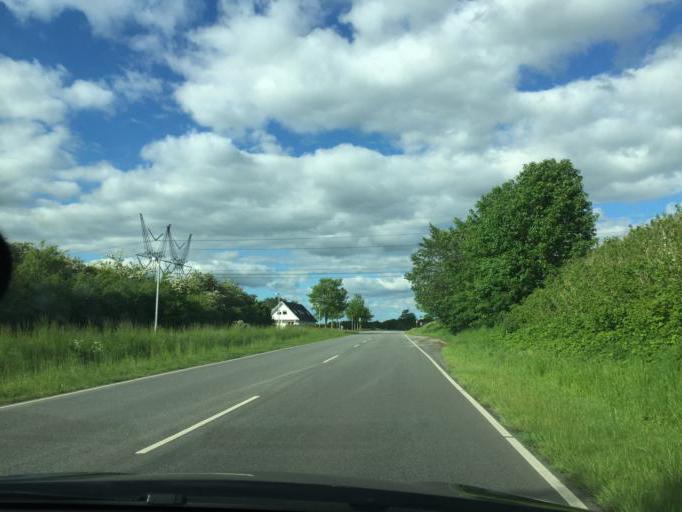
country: DK
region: South Denmark
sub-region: Odense Kommune
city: Bellinge
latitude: 55.3430
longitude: 10.3247
